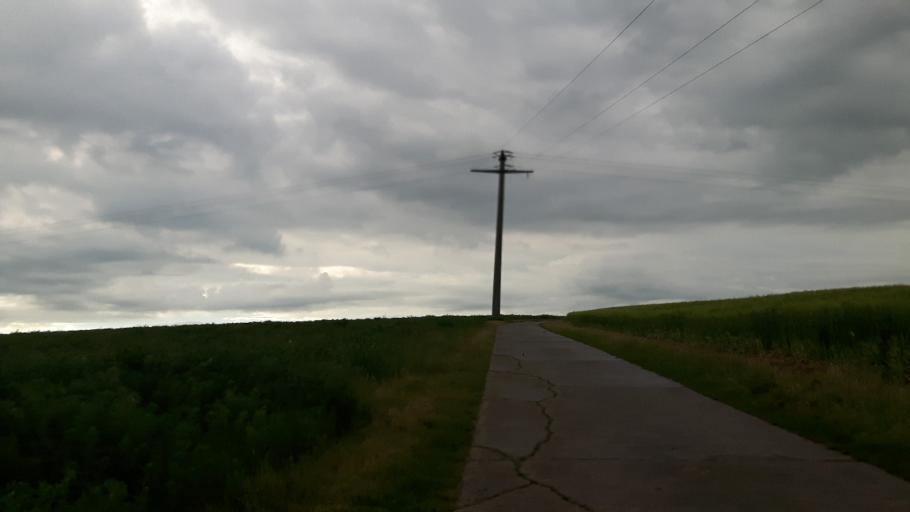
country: DE
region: Bavaria
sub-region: Regierungsbezirk Unterfranken
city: Stadtlauringen
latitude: 50.1775
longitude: 10.3642
